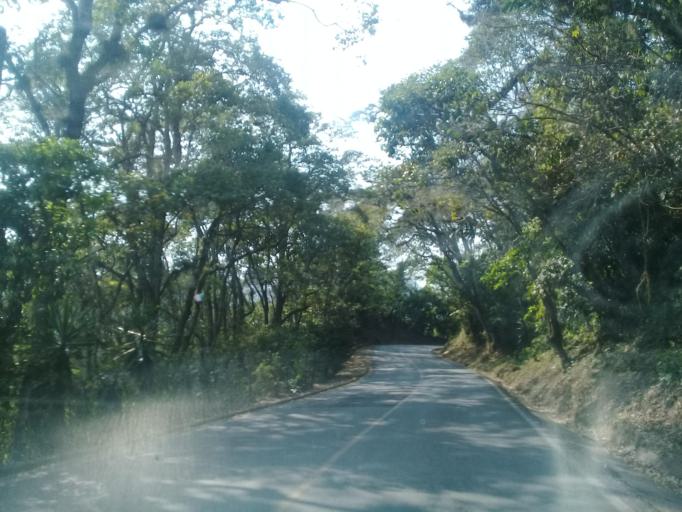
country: MX
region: Veracruz
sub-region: Ixtaczoquitlan
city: Campo Chico
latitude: 18.8401
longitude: -97.0264
